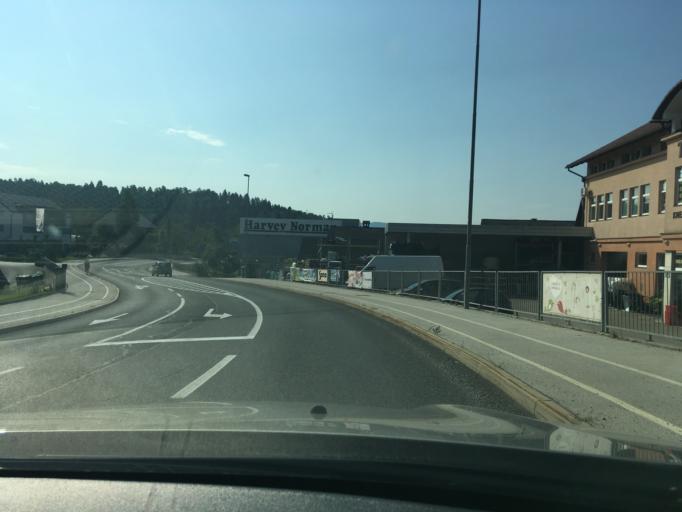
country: SI
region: Novo Mesto
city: Novo Mesto
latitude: 45.8306
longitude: 15.1558
